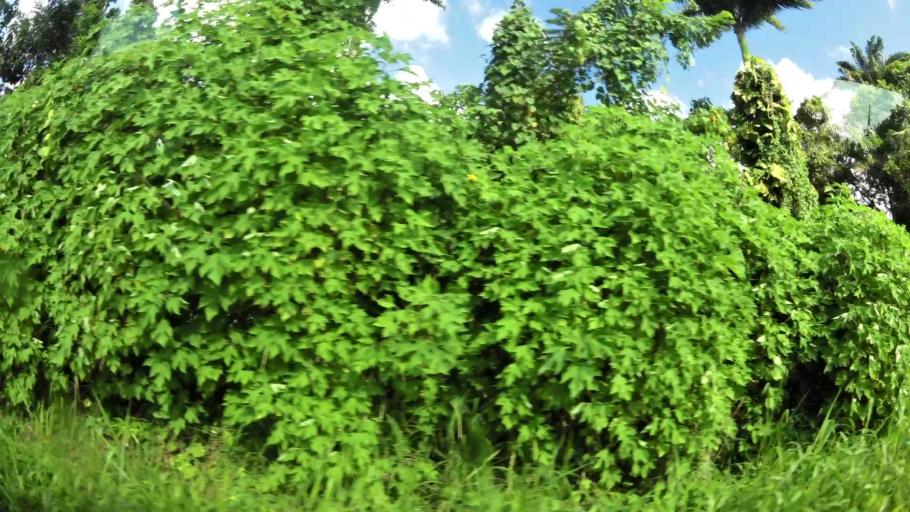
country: MQ
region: Martinique
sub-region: Martinique
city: Fort-de-France
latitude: 14.6462
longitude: -61.0796
